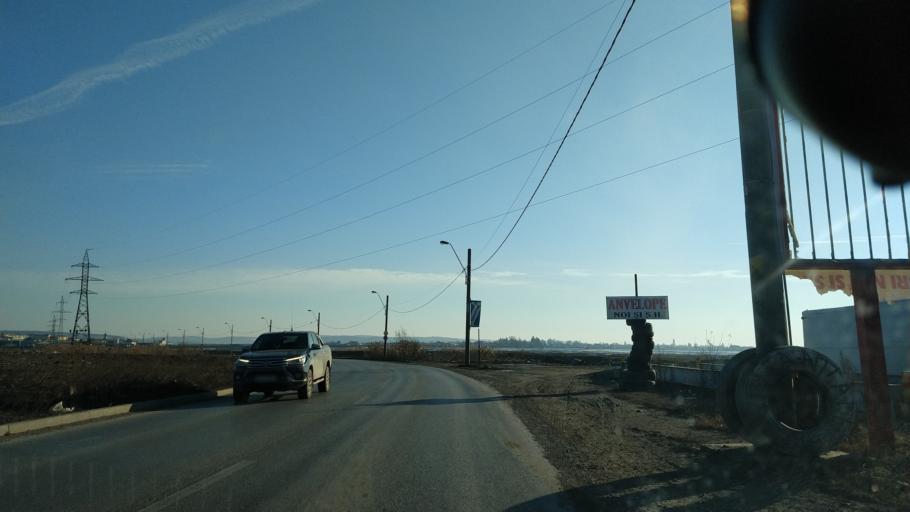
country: RO
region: Neamt
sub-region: Municipiul Roman
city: Roman
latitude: 46.9238
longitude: 26.9102
